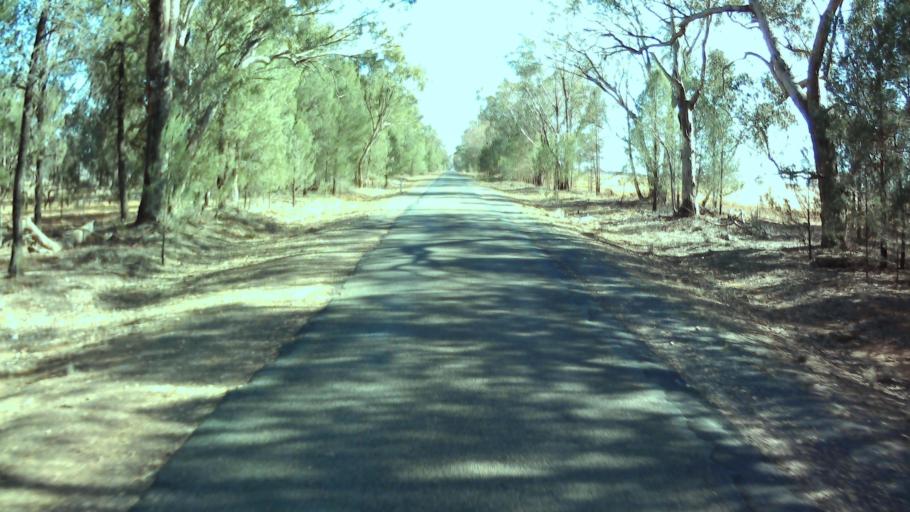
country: AU
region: New South Wales
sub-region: Weddin
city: Grenfell
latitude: -33.8102
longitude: 147.9541
